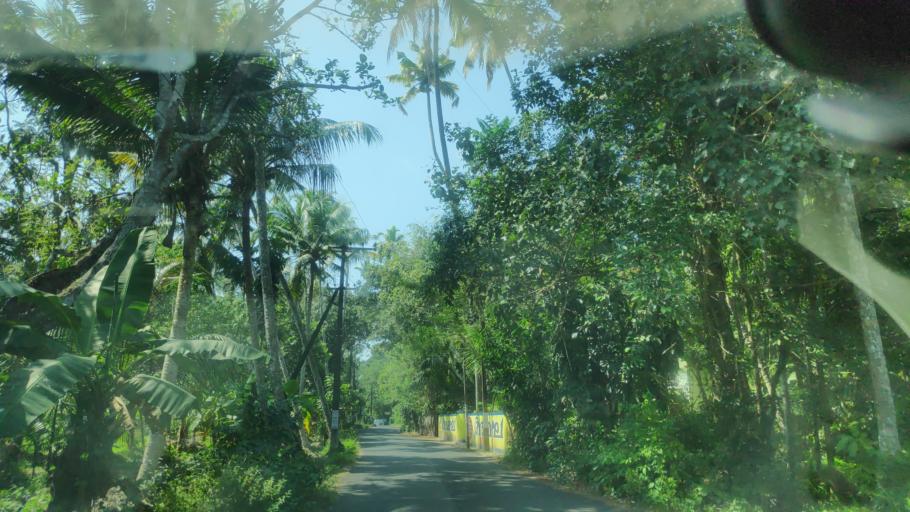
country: IN
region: Kerala
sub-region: Alappuzha
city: Vayalar
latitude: 9.6633
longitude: 76.3090
